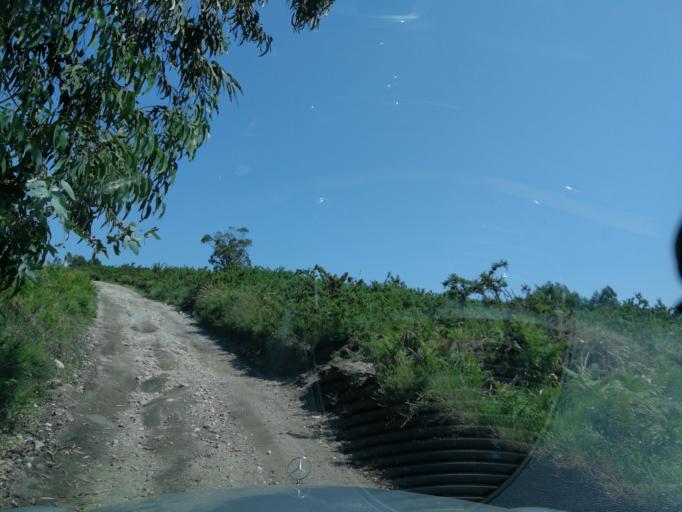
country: PT
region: Braga
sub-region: Povoa de Lanhoso
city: Povoa de Lanhoso
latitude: 41.5635
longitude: -8.3403
